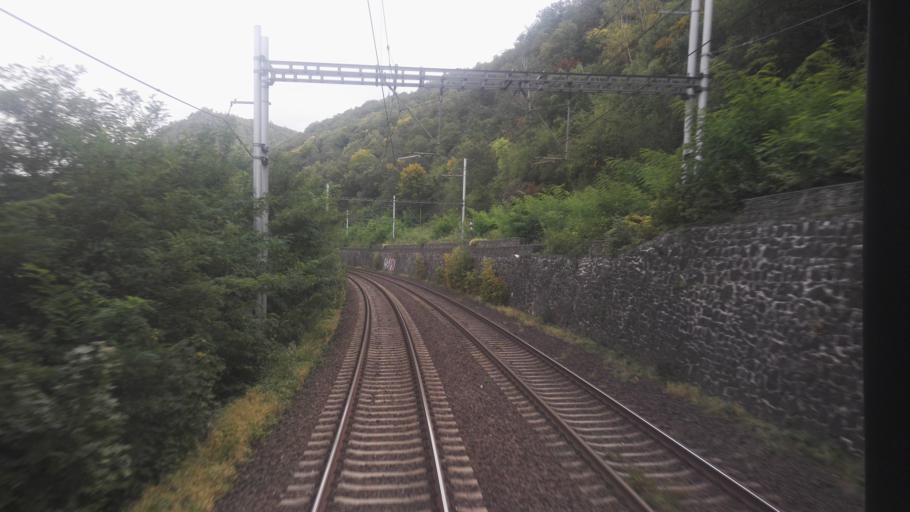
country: CZ
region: Central Bohemia
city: Rez
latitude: 50.1687
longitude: 14.3535
